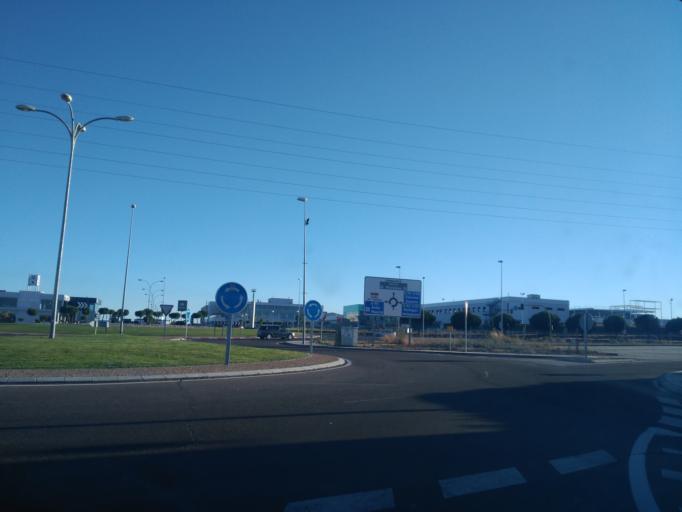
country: ES
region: Castille and Leon
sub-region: Provincia de Salamanca
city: Carbajosa de la Sagrada
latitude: 40.9433
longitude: -5.6556
